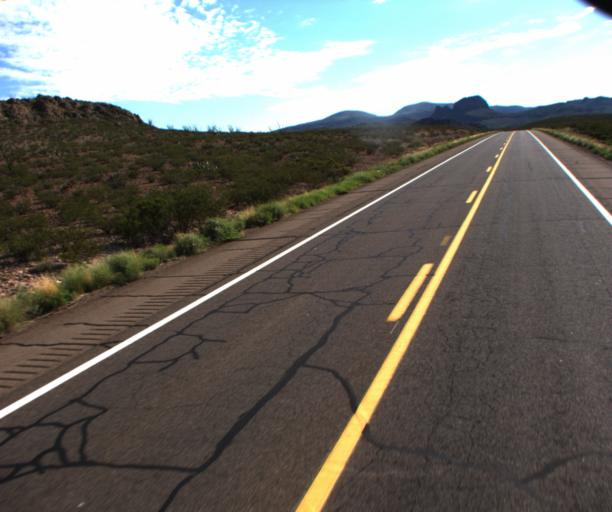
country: US
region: Arizona
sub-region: Greenlee County
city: Clifton
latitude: 32.8434
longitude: -109.4179
